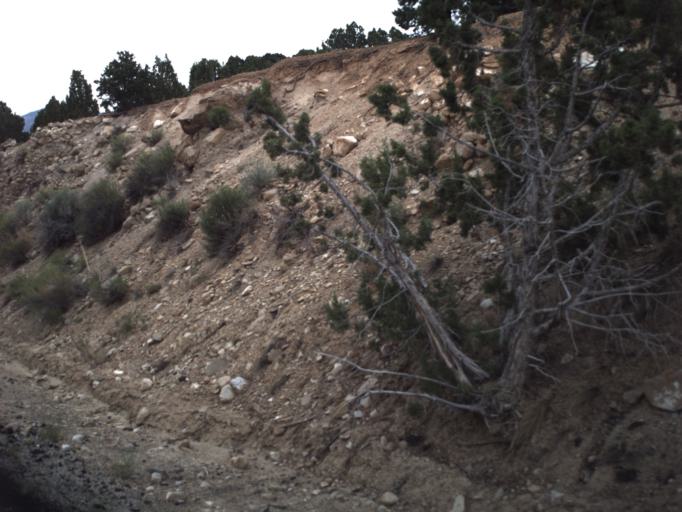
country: US
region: Utah
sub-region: Carbon County
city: East Carbon City
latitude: 39.4866
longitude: -110.4040
